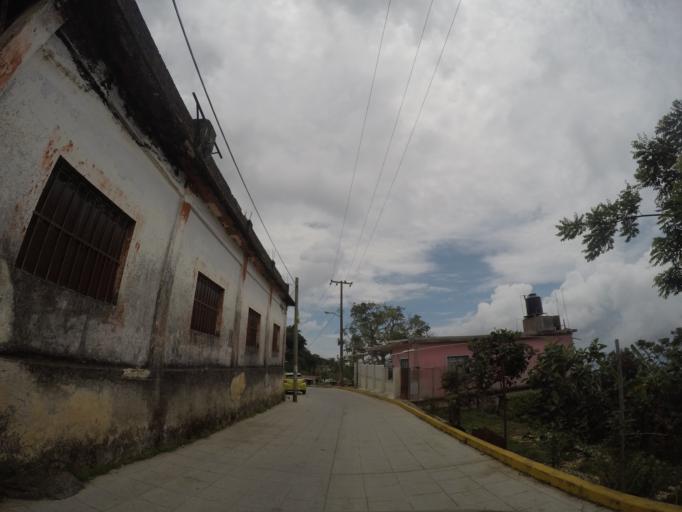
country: MX
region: Oaxaca
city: Pluma Hidalgo
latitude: 15.9249
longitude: -96.4189
